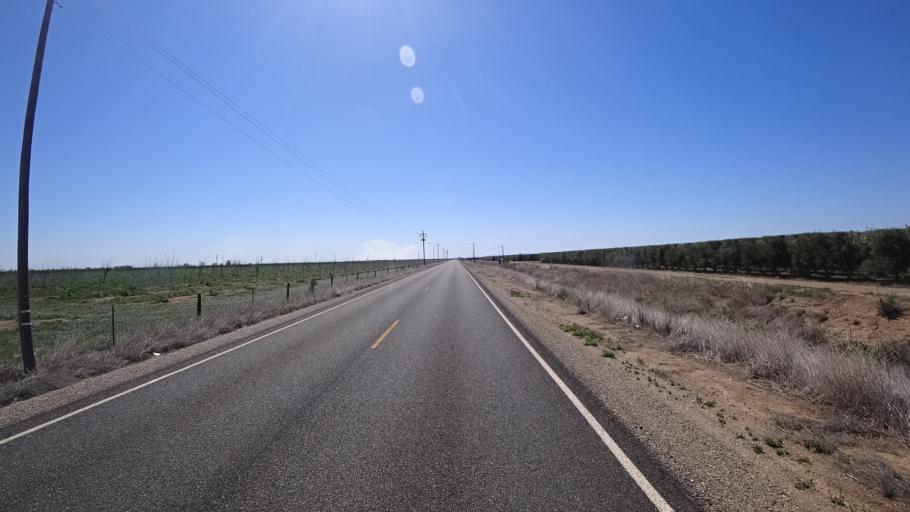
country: US
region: California
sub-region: Glenn County
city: Willows
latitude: 39.6006
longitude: -122.2498
